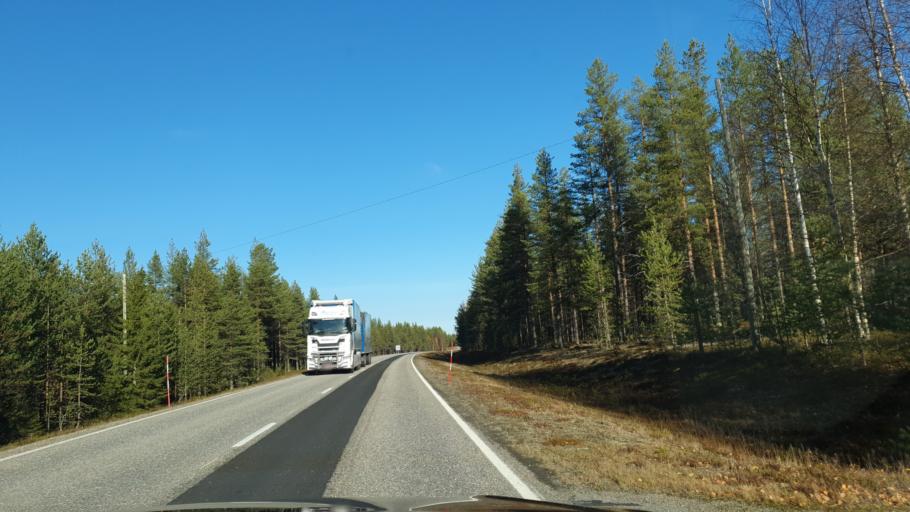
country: FI
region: Lapland
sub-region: Tunturi-Lappi
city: Kittilae
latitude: 67.3146
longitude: 24.9102
